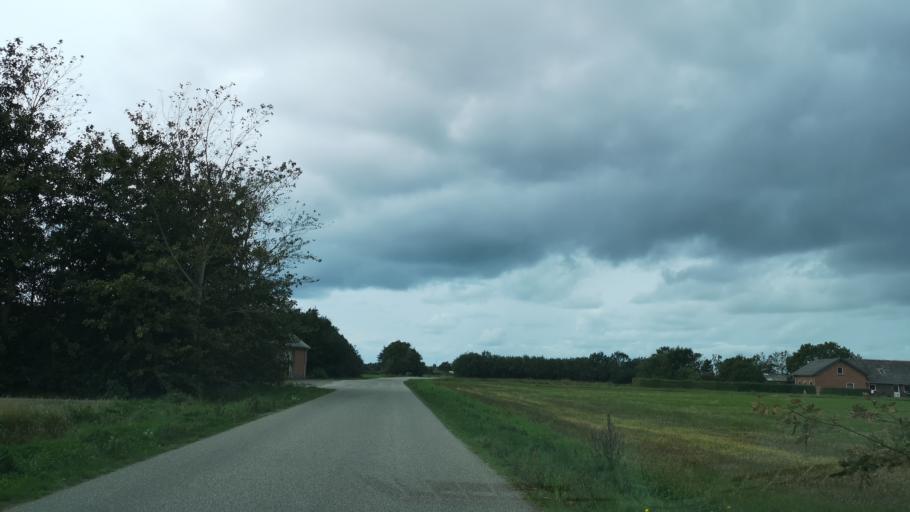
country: DK
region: South Denmark
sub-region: Varde Kommune
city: Oksbol
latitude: 55.8363
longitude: 8.3069
